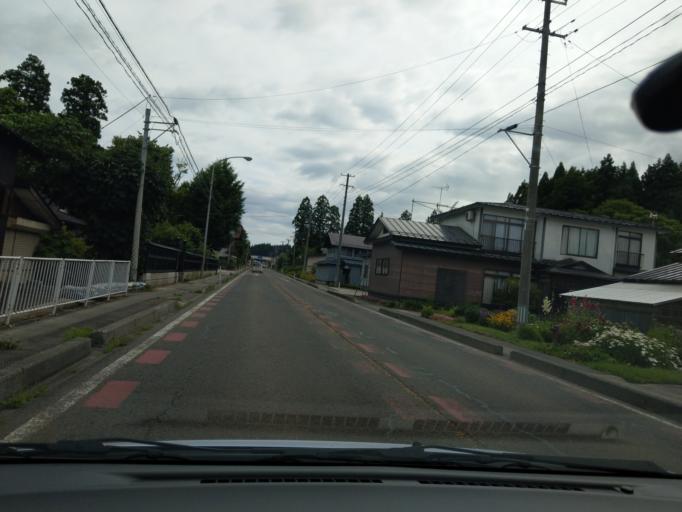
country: JP
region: Akita
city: Yokotemachi
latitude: 39.3667
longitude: 140.5670
